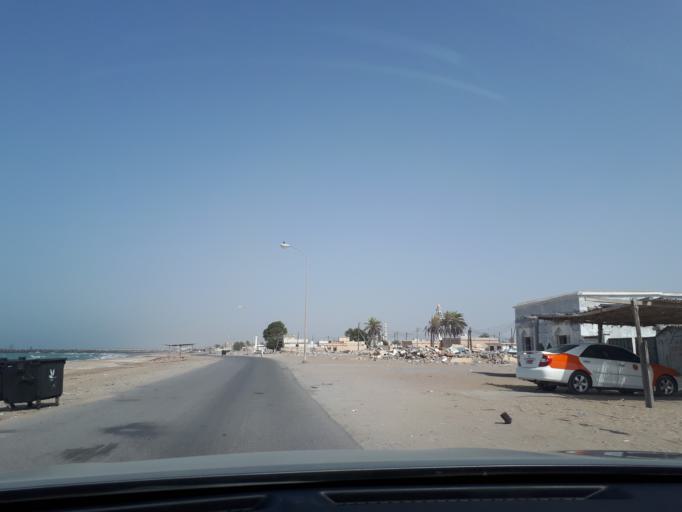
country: OM
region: Al Batinah
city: Barka'
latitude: 23.7114
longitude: 57.8828
